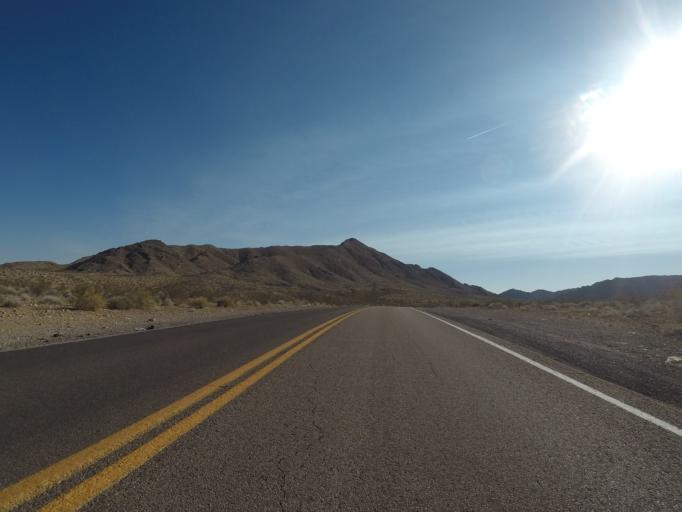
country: US
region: Nevada
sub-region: Clark County
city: Moapa Valley
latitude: 36.4176
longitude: -114.5965
